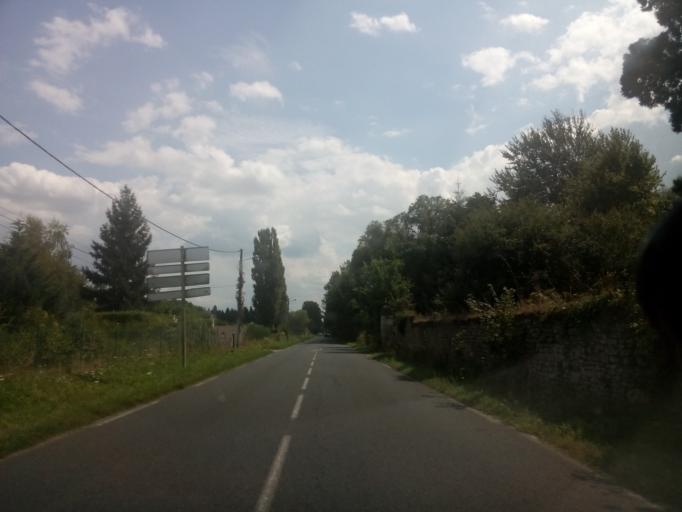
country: FR
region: Centre
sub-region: Departement d'Indre-et-Loire
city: Cheille
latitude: 47.2704
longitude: 0.4283
